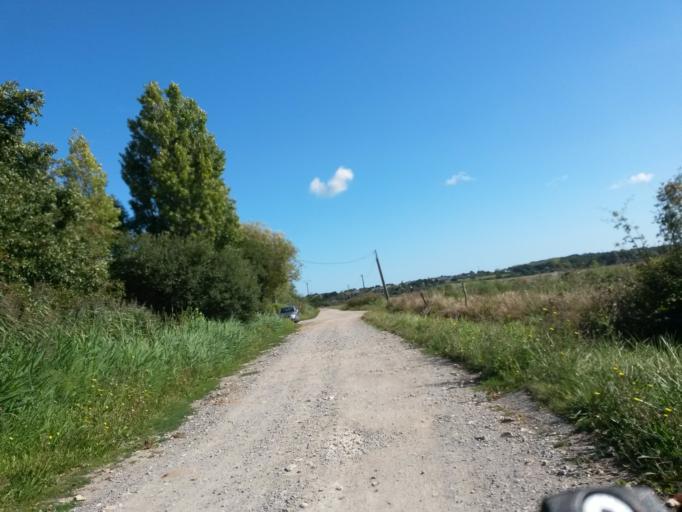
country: FR
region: Pays de la Loire
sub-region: Departement de la Loire-Atlantique
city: Guerande
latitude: 47.3081
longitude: -2.4412
